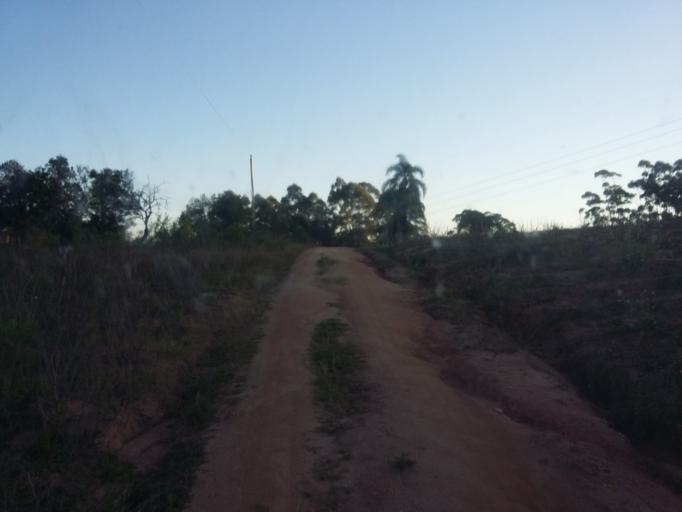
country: BR
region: Rio Grande do Sul
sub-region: Camaqua
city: Camaqua
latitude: -30.7052
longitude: -51.7669
